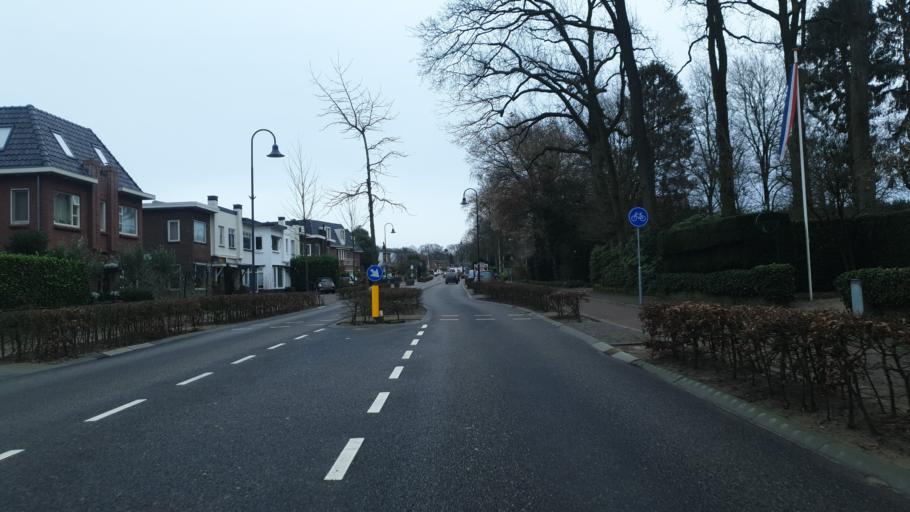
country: NL
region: Gelderland
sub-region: Gemeente Groesbeek
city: Berg en Dal
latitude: 51.8266
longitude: 5.9069
